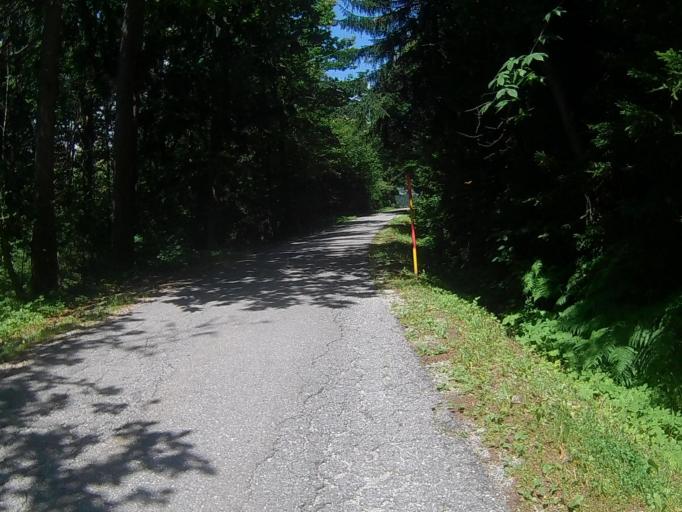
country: SI
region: Race-Fram
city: Morje
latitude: 46.4795
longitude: 15.5856
